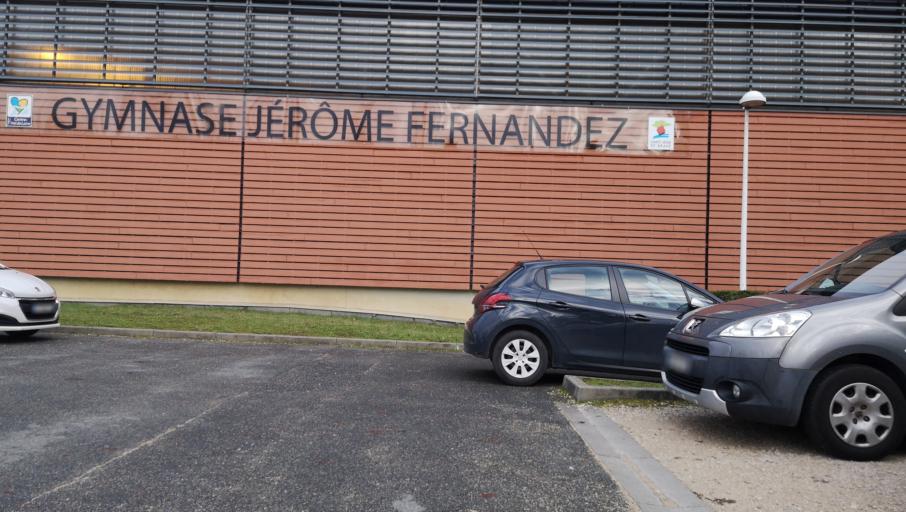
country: FR
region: Centre
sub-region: Departement du Loiret
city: Saint-Jean-de-Braye
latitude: 47.9084
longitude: 1.9665
